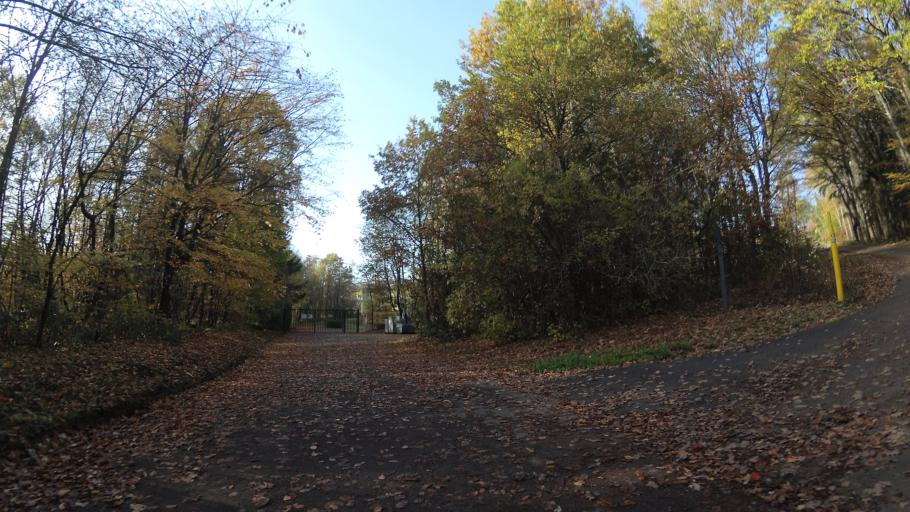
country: DE
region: Saarland
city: Bexbach
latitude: 49.3682
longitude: 7.2376
